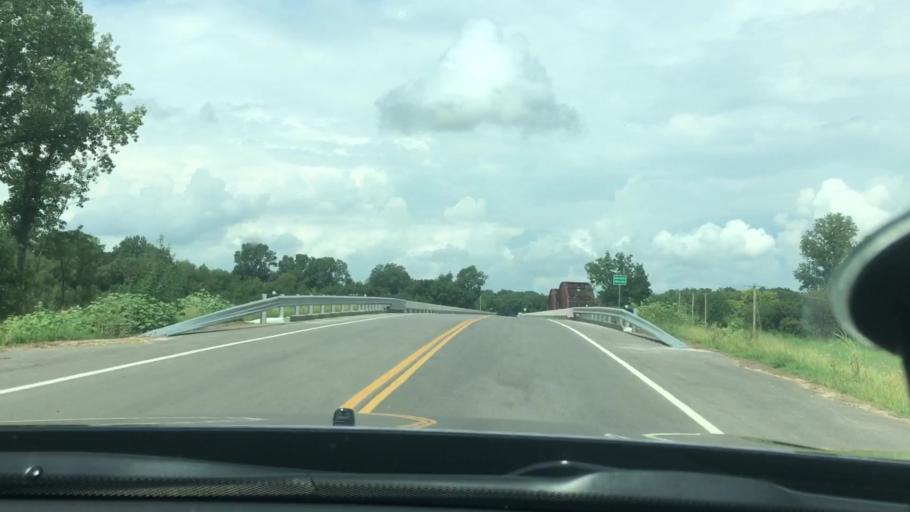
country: US
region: Oklahoma
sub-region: Carter County
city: Dickson
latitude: 34.2284
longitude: -96.9065
